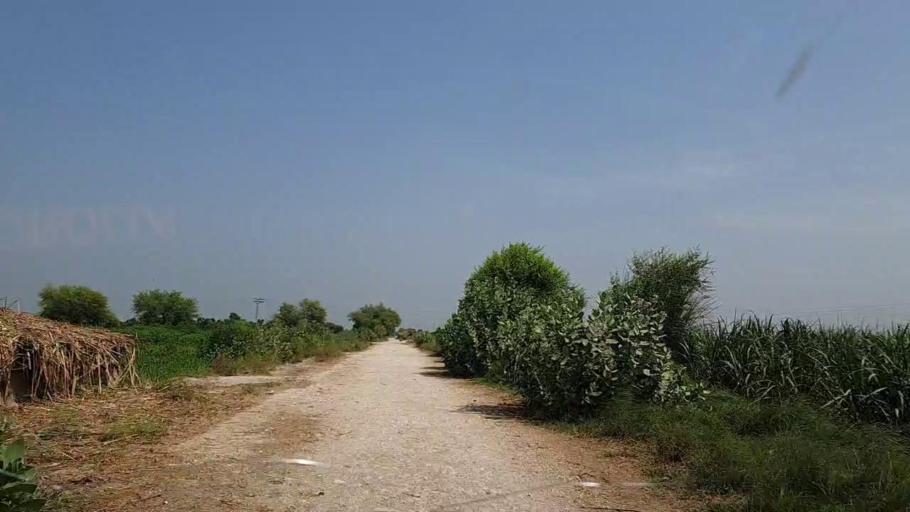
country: PK
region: Sindh
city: Adilpur
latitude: 27.8388
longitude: 69.2790
